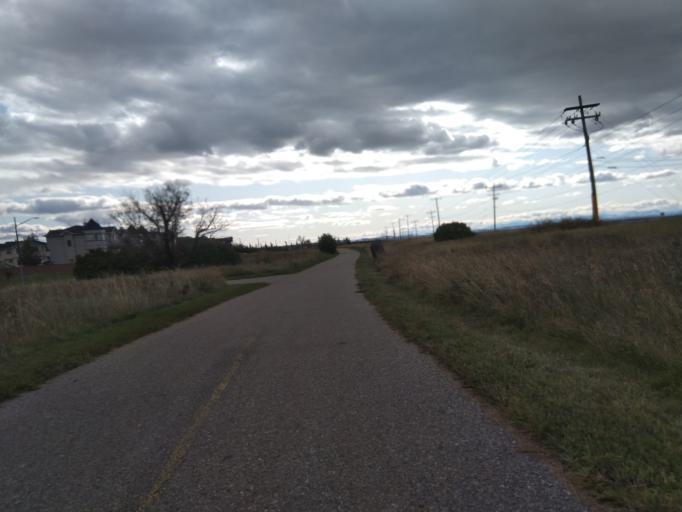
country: CA
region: Alberta
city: Calgary
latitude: 51.0308
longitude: -113.9947
